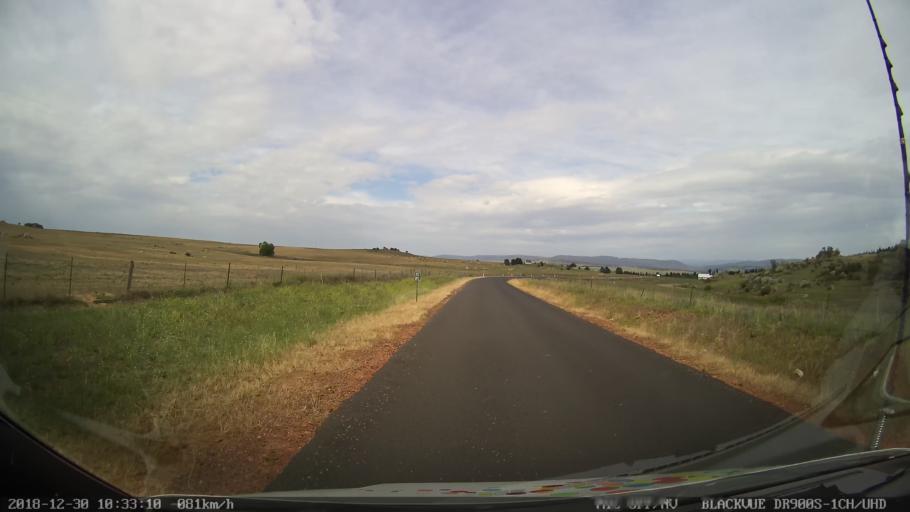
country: AU
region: New South Wales
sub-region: Snowy River
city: Berridale
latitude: -36.4992
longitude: 148.8563
